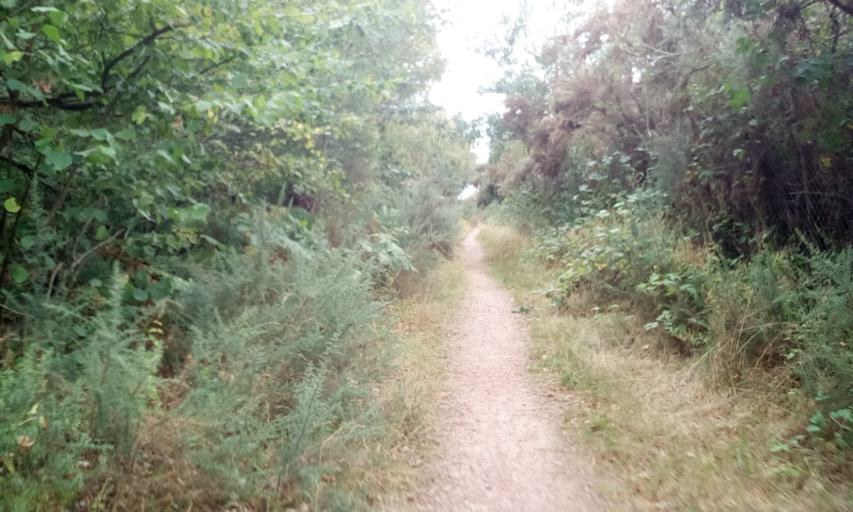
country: FR
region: Lower Normandy
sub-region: Departement du Calvados
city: Mouen
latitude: 49.1388
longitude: -0.4814
